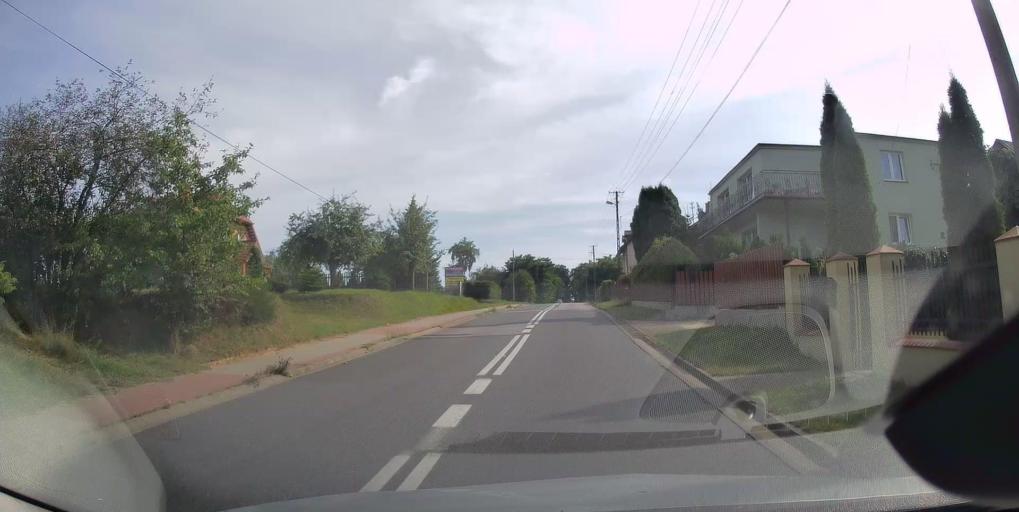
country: PL
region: Lodz Voivodeship
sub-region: Powiat tomaszowski
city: Tomaszow Mazowiecki
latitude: 51.4841
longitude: 19.9884
